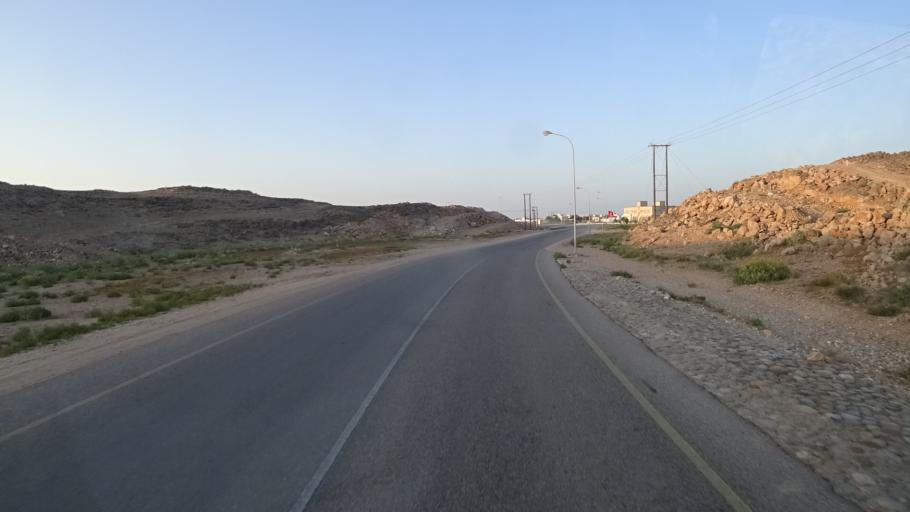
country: OM
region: Ash Sharqiyah
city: Sur
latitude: 22.5066
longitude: 59.7928
